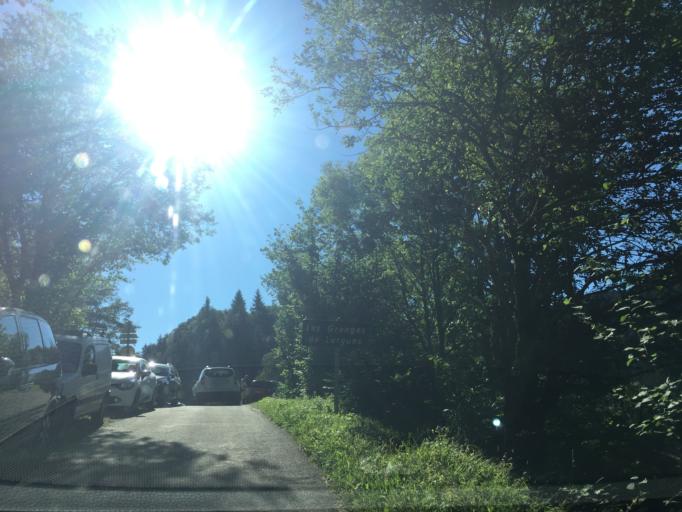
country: FR
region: Midi-Pyrenees
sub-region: Departement des Hautes-Pyrenees
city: Saint-Lary-Soulan
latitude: 42.8513
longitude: 0.2760
